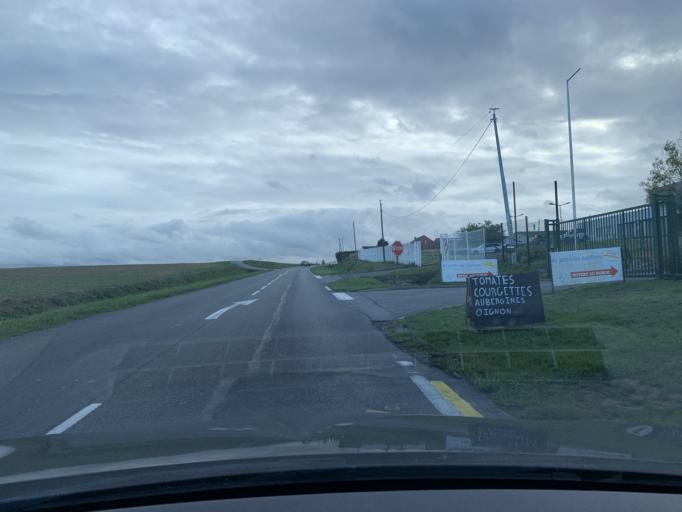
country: FR
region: Nord-Pas-de-Calais
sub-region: Departement du Nord
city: Proville
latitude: 50.1454
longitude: 3.2141
